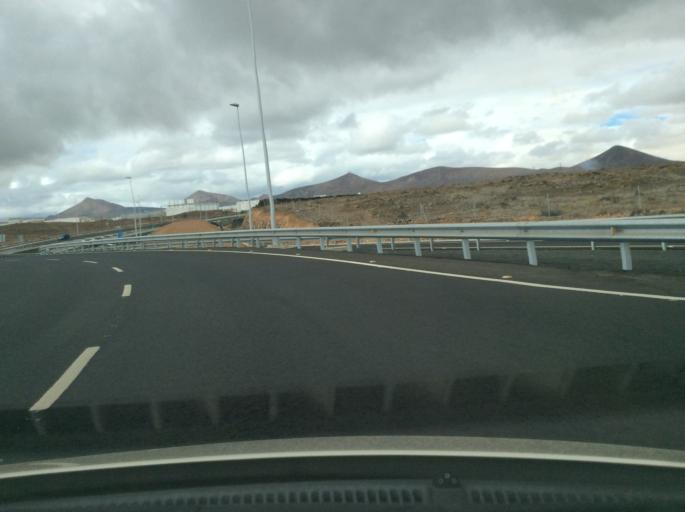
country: ES
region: Canary Islands
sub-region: Provincia de Las Palmas
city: Arrecife
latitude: 28.9777
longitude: -13.5308
